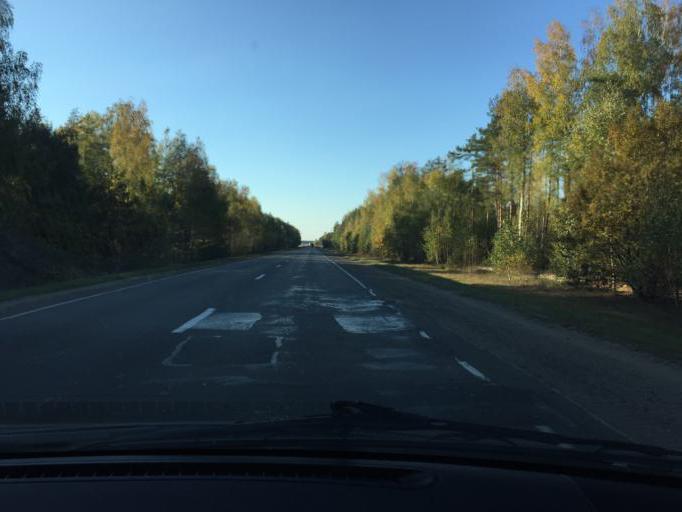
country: BY
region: Brest
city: Luninyets
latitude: 52.2700
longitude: 26.9972
